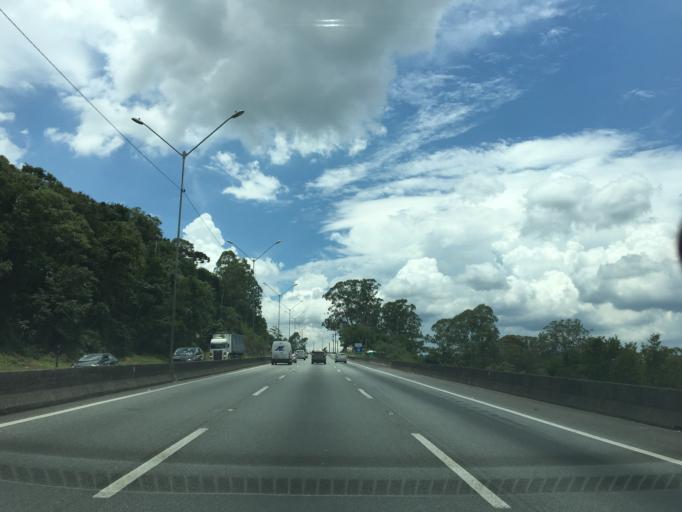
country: BR
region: Sao Paulo
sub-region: Mairipora
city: Mairipora
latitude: -23.3082
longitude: -46.5784
